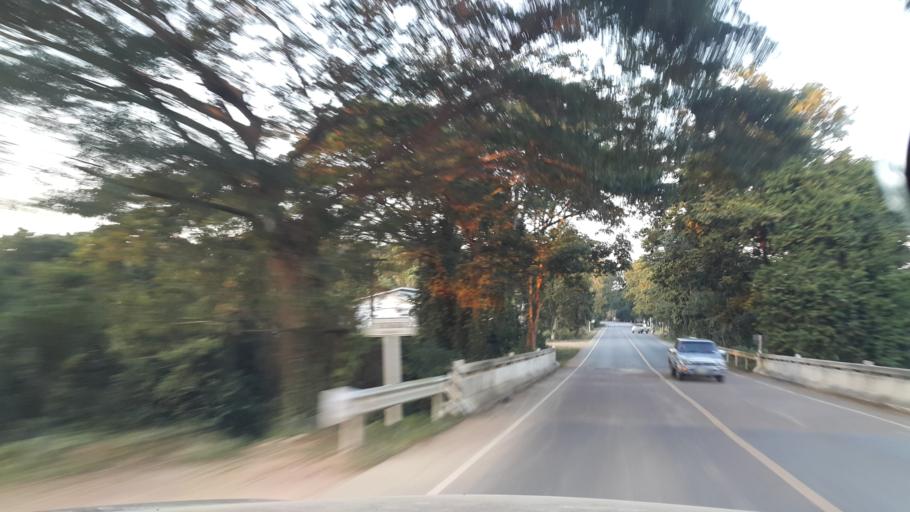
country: TH
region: Phrae
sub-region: Amphoe Wang Chin
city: Wang Chin
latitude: 17.8643
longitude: 99.6223
